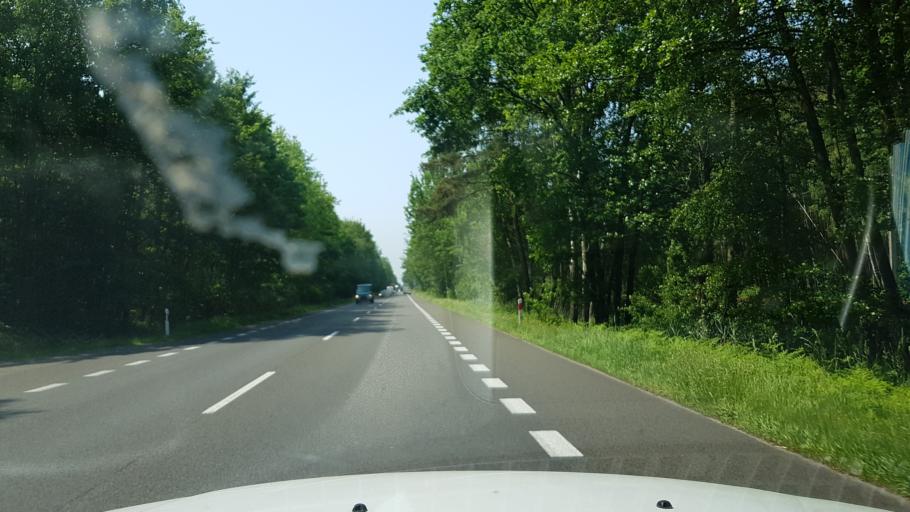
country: PL
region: West Pomeranian Voivodeship
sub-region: Powiat kamienski
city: Miedzyzdroje
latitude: 53.9037
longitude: 14.3788
